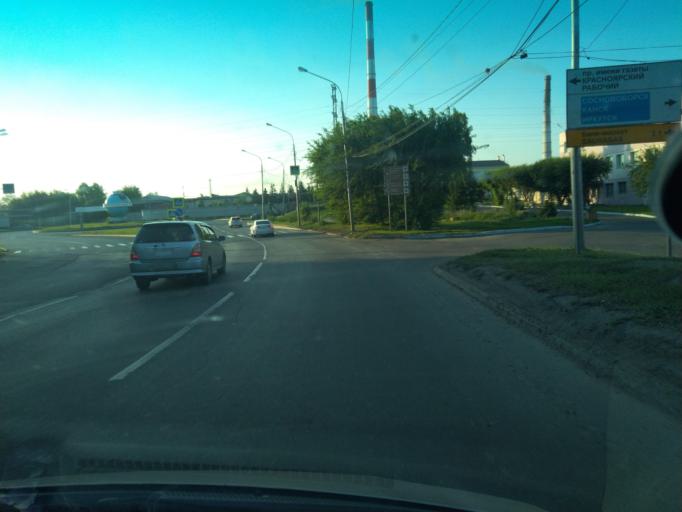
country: RU
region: Krasnoyarskiy
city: Berezovka
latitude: 56.0179
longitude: 93.0318
